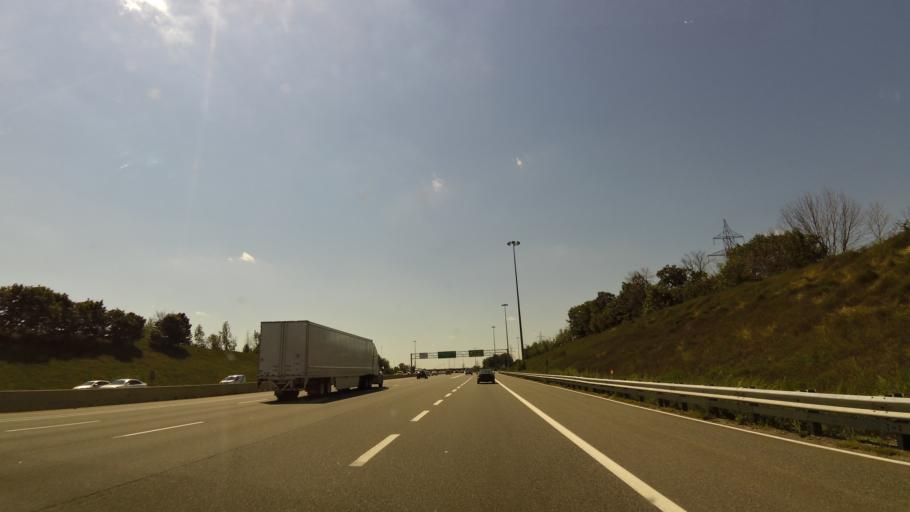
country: CA
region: Ontario
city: Mississauga
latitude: 43.5580
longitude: -79.6909
